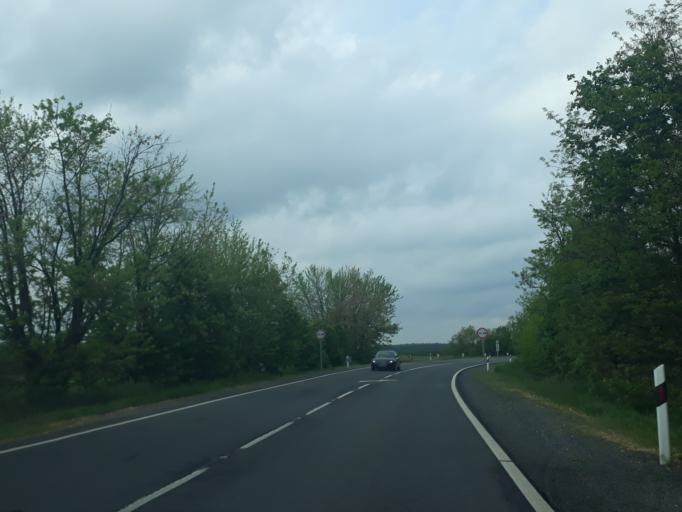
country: HU
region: Szabolcs-Szatmar-Bereg
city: Patroha
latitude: 48.1580
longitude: 22.0276
